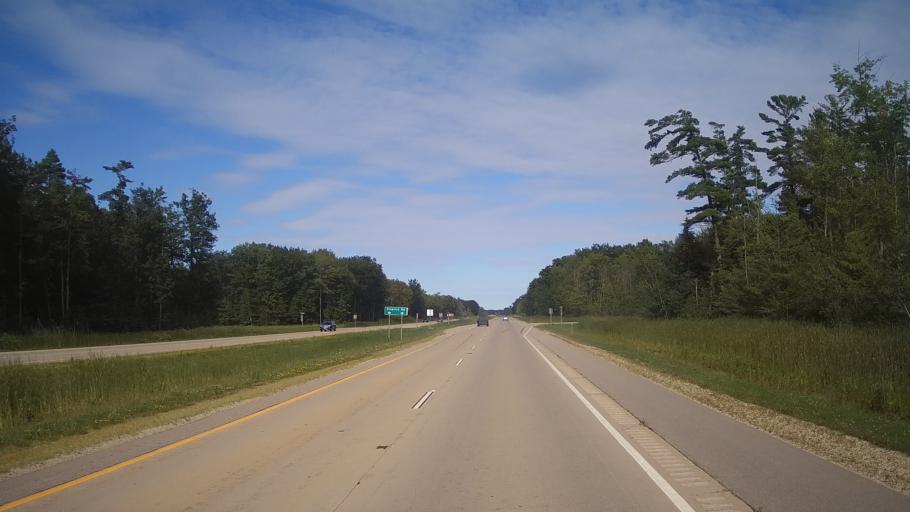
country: US
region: Wisconsin
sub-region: Oconto County
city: Oconto
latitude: 44.8074
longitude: -87.9687
